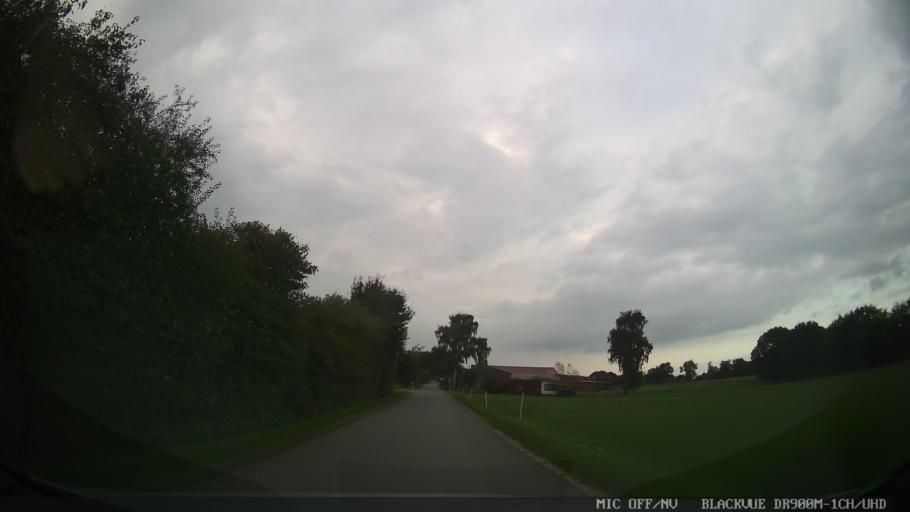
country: DE
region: Schleswig-Holstein
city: Gromitz
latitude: 54.1802
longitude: 10.9553
